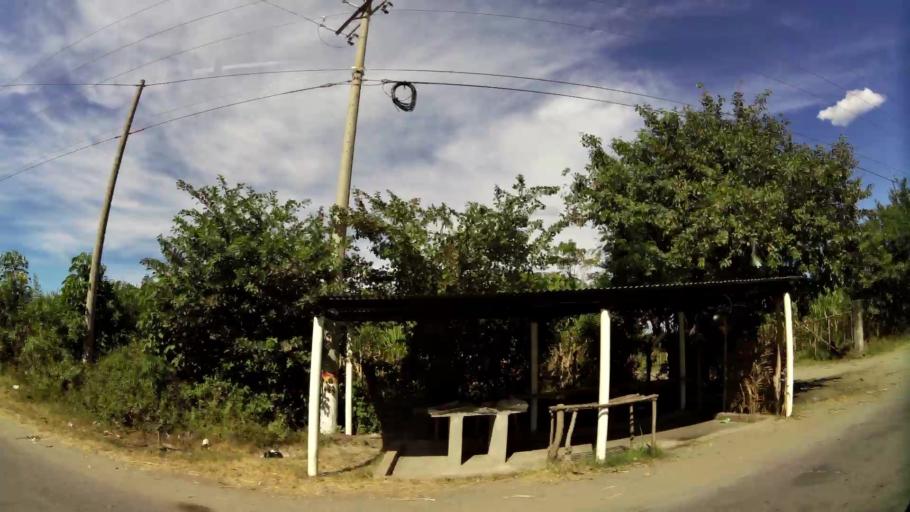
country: SV
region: San Salvador
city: Aguilares
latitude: 13.9622
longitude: -89.1646
